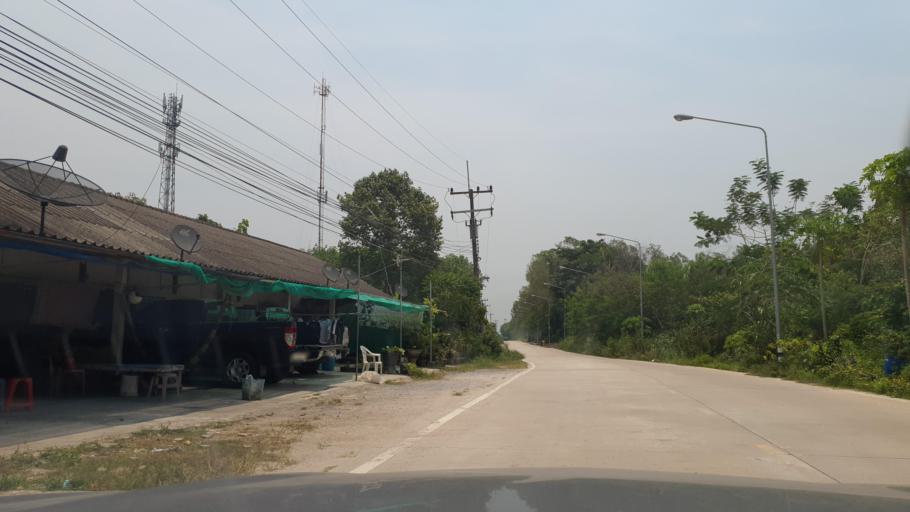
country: TH
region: Rayong
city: Nikhom Phattana
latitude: 12.7920
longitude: 101.1556
